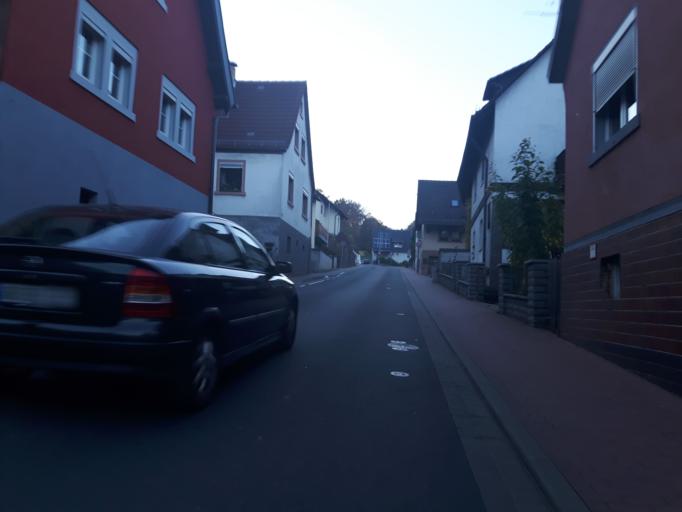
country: DE
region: Bavaria
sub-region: Regierungsbezirk Unterfranken
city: Heimbuchenthal
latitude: 49.8826
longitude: 9.2917
